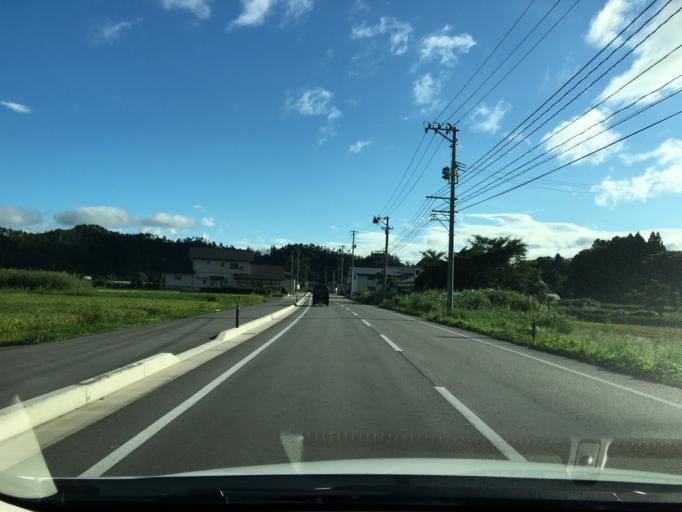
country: JP
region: Yamagata
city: Yonezawa
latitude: 37.9396
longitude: 140.1685
